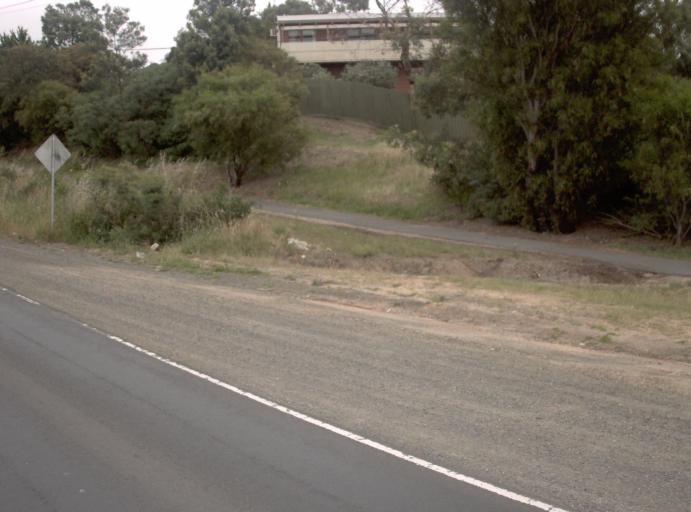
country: AU
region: Victoria
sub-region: Casey
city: Hallam
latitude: -38.0247
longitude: 145.2695
